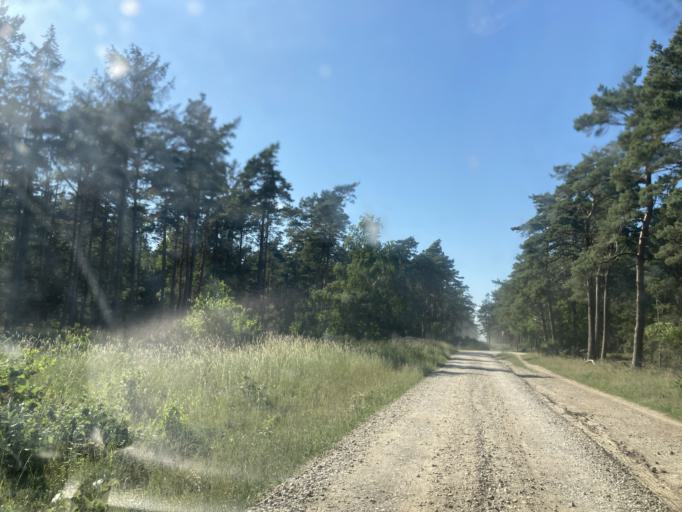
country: DK
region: Capital Region
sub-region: Halsnaes Kommune
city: Frederiksvaerk
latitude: 56.0184
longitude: 12.0091
